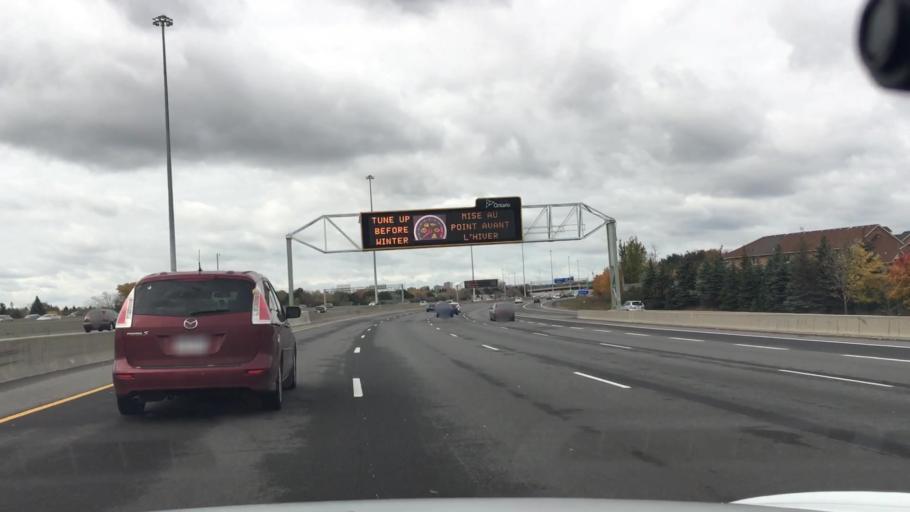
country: CA
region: Ontario
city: Scarborough
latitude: 43.7958
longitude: -79.1535
